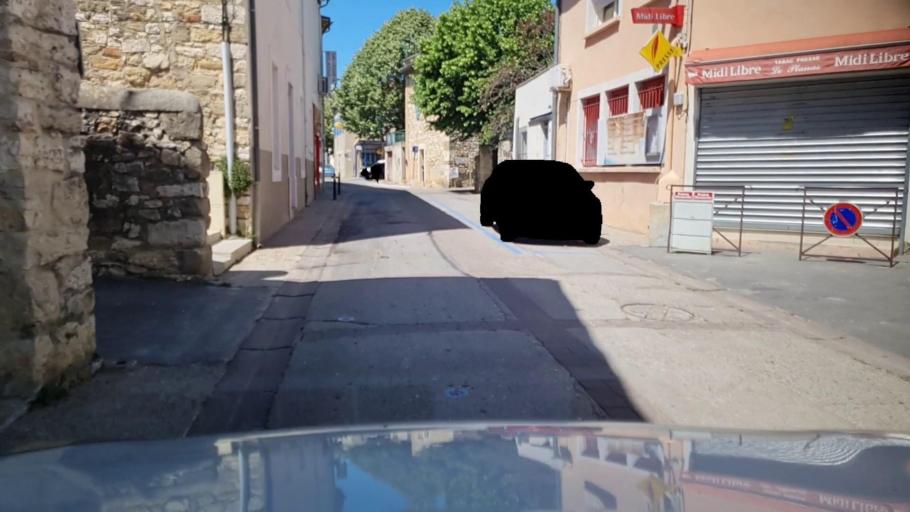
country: FR
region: Languedoc-Roussillon
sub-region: Departement du Gard
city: Saint-Mamert-du-Gard
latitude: 43.8867
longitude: 4.1890
